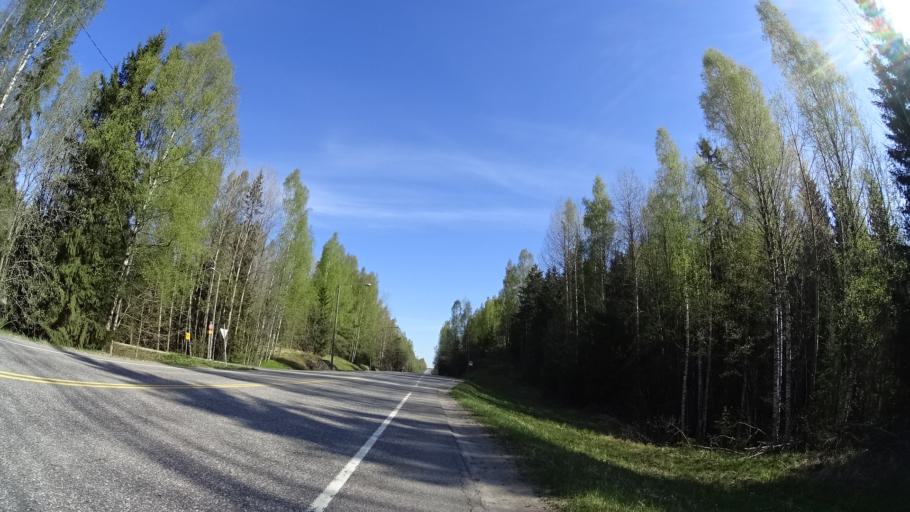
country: FI
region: Uusimaa
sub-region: Helsinki
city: Nurmijaervi
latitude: 60.3739
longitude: 24.8057
